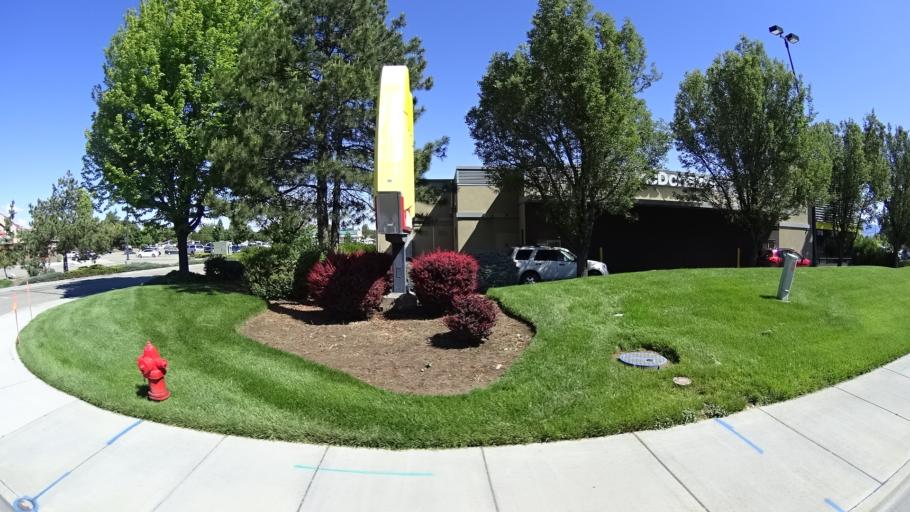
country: US
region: Idaho
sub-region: Ada County
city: Meridian
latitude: 43.6196
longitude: -116.3730
